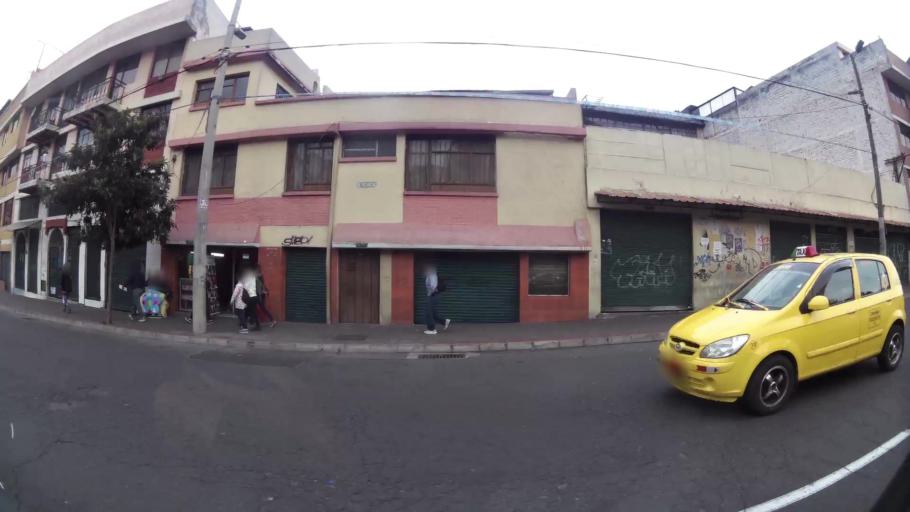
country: EC
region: Pichincha
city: Quito
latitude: -0.2250
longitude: -78.5069
